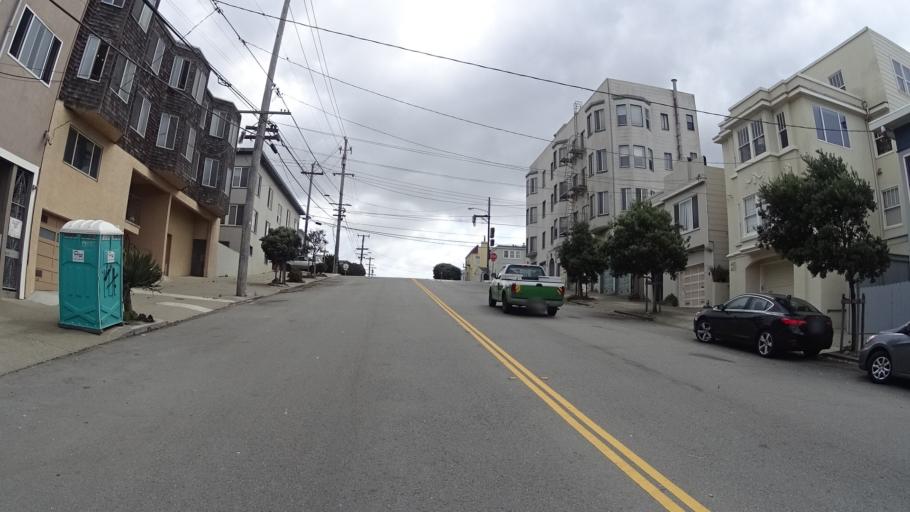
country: US
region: California
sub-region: San Mateo County
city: Daly City
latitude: 37.7752
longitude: -122.5088
